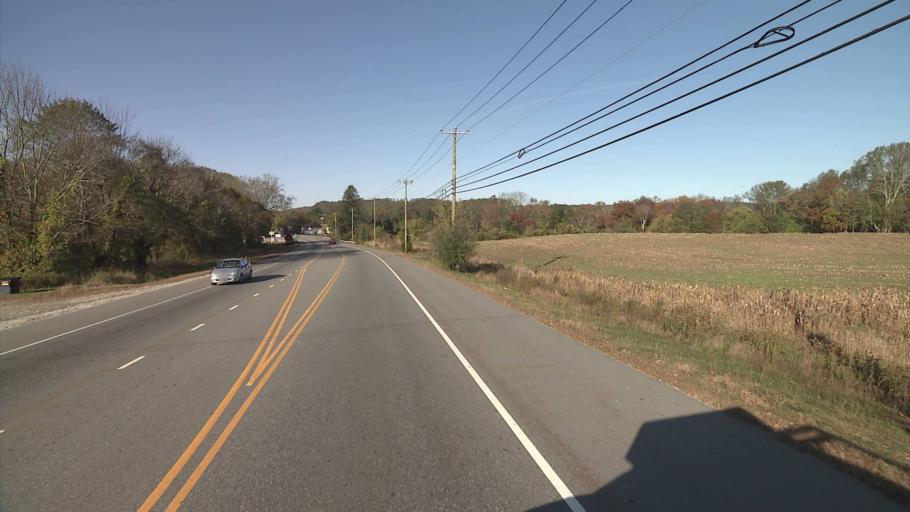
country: US
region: Connecticut
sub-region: Windham County
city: East Brooklyn
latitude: 41.7967
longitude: -71.9280
